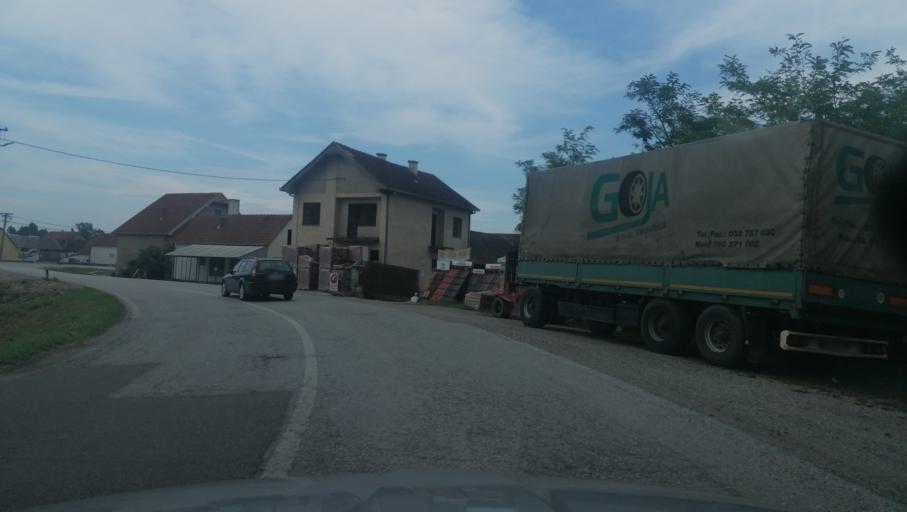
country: RS
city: Klenje
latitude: 44.8085
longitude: 19.4362
